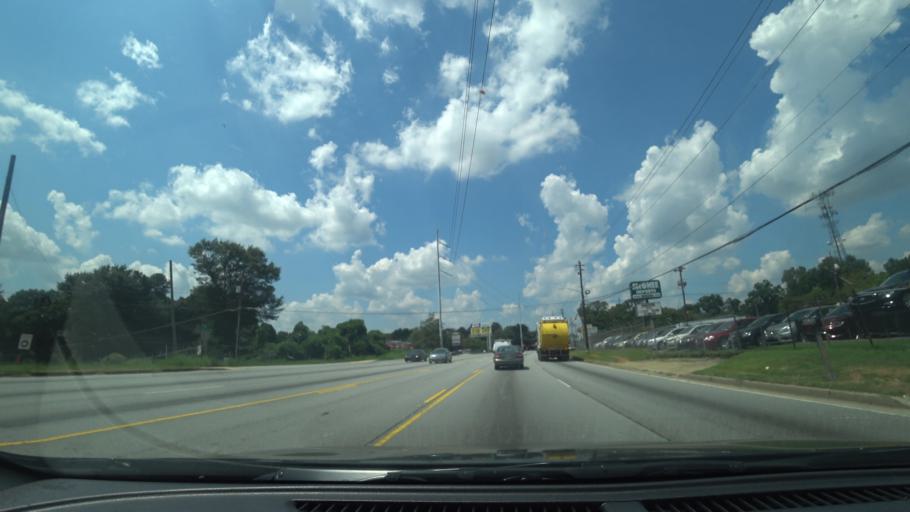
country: US
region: Georgia
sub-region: DeKalb County
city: Belvedere Park
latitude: 33.7356
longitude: -84.2143
